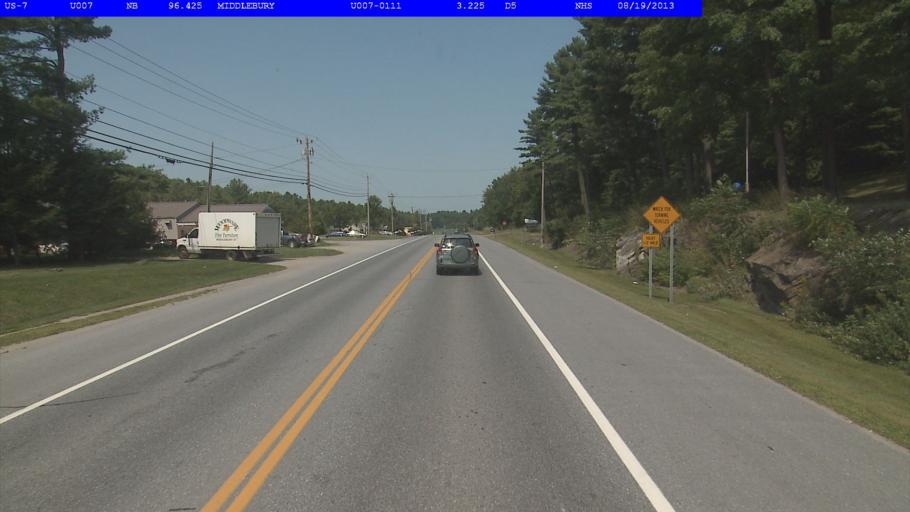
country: US
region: Vermont
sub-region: Addison County
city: Middlebury (village)
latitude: 43.9947
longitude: -73.1436
